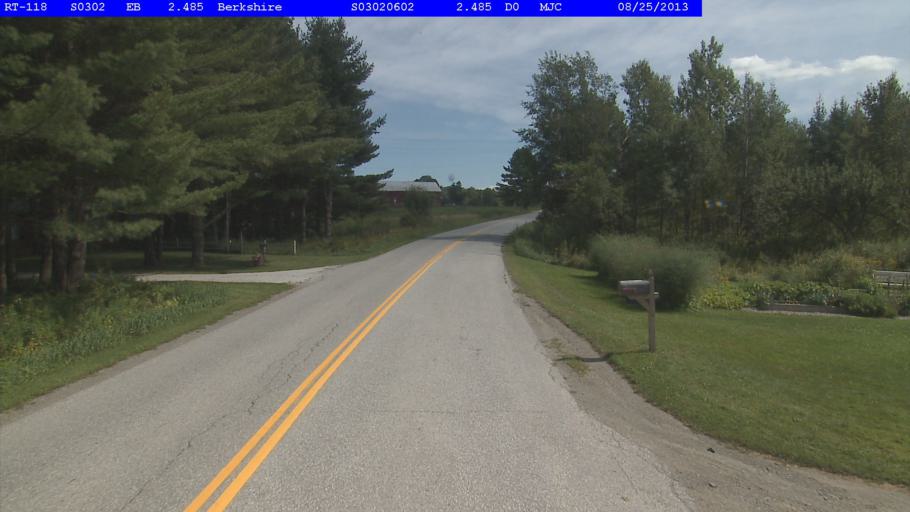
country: US
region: Vermont
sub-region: Franklin County
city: Enosburg Falls
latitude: 44.9749
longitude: -72.7683
